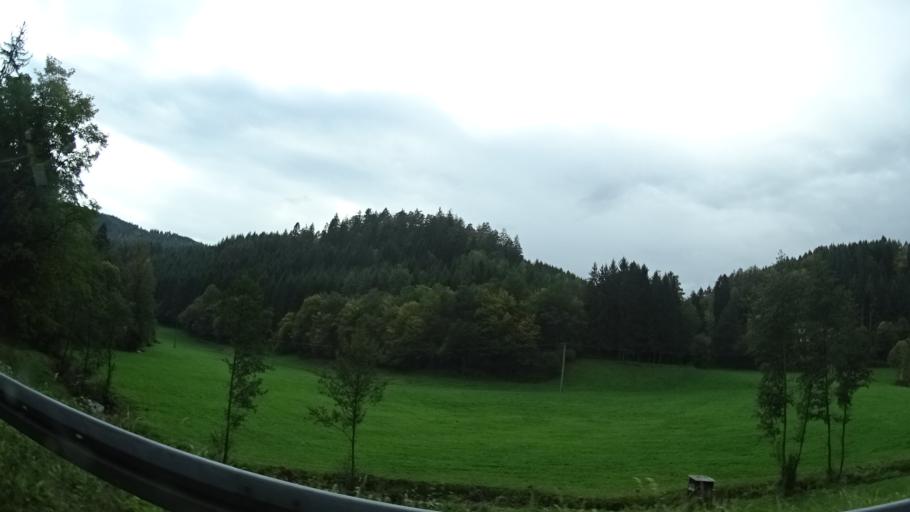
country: DE
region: Bavaria
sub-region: Regierungsbezirk Unterfranken
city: Kirchzell
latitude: 49.6169
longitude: 9.1465
